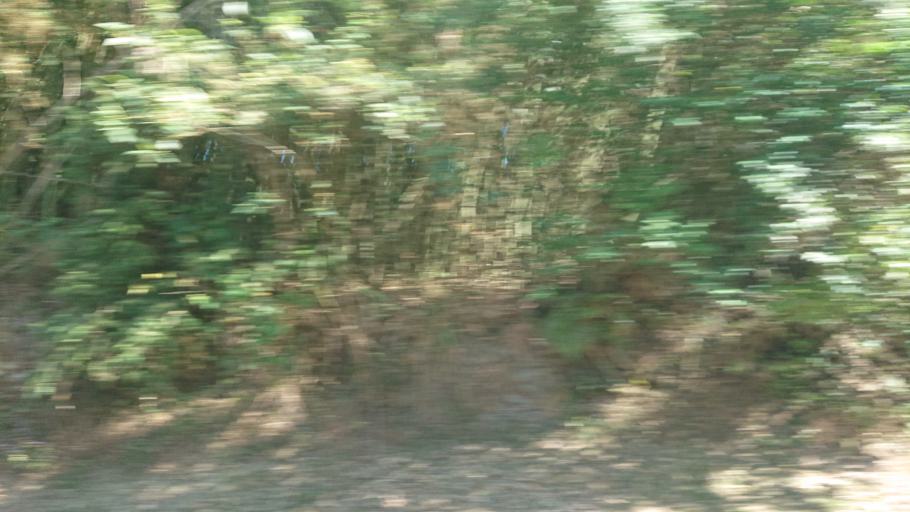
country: TW
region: Taiwan
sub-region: Chiayi
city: Jiayi Shi
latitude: 23.4700
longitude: 120.7096
